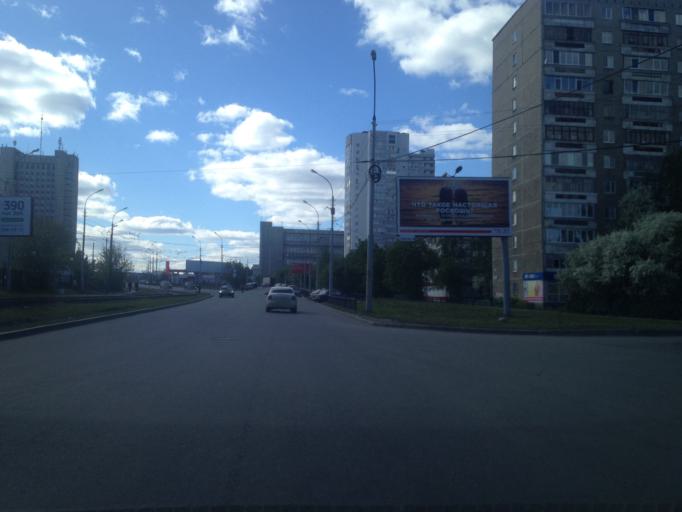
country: RU
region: Sverdlovsk
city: Sovkhoznyy
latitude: 56.8128
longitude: 60.5566
